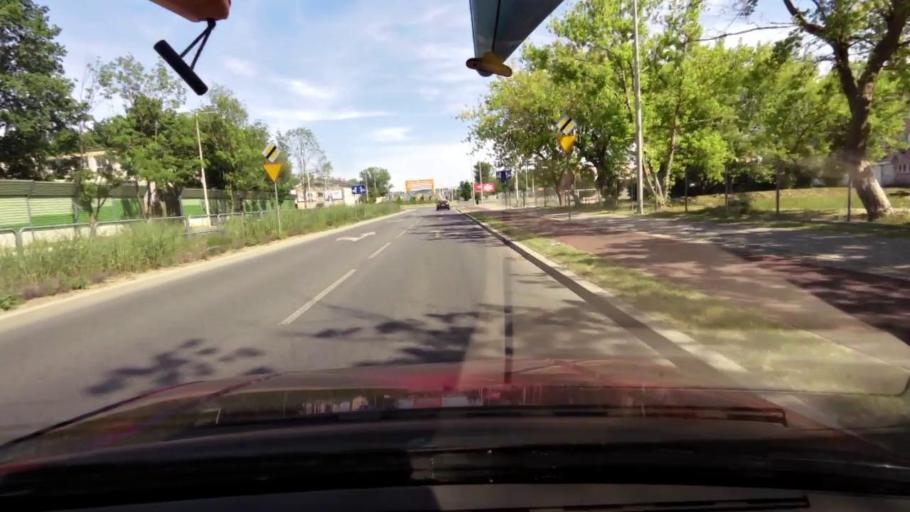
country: PL
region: Pomeranian Voivodeship
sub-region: Powiat slupski
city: Kobylnica
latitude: 54.4558
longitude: 17.0056
